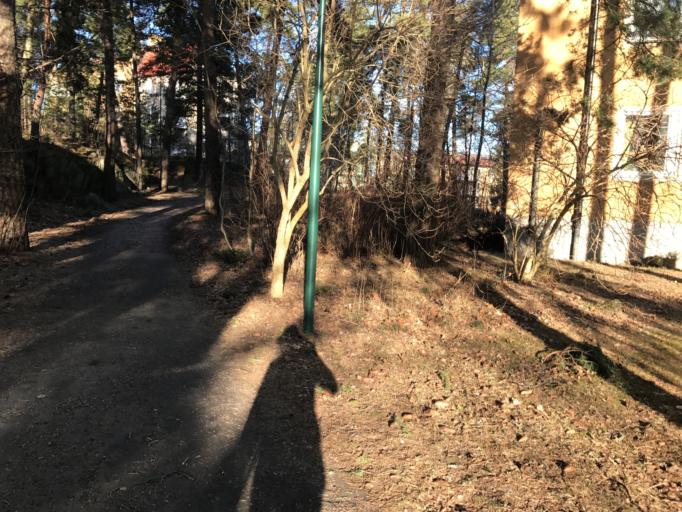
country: SE
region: Stockholm
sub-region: Nacka Kommun
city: Nacka
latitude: 59.2792
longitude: 18.1241
